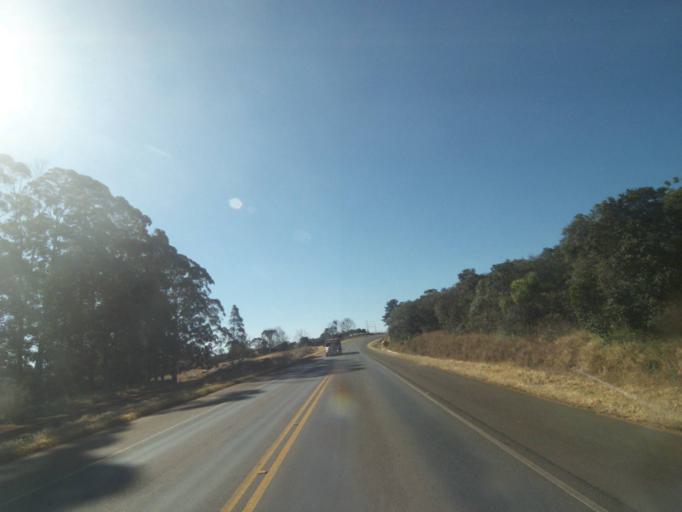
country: BR
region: Parana
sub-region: Tibagi
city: Tibagi
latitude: -24.6984
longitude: -50.4462
